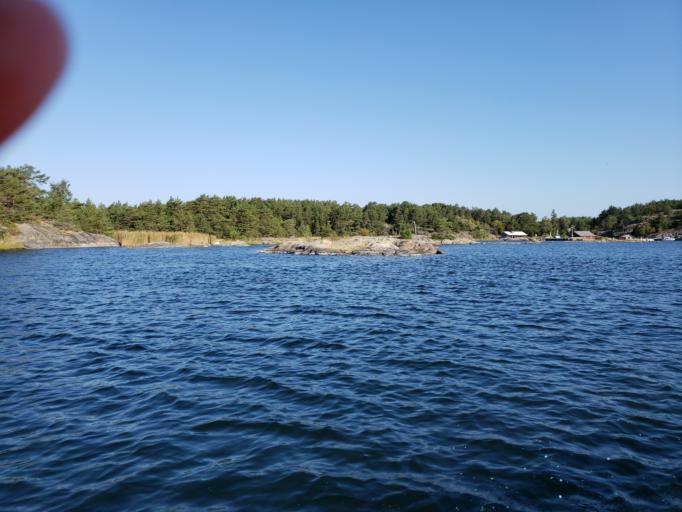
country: FI
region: Varsinais-Suomi
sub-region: Aboland-Turunmaa
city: Dragsfjaerd
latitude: 59.9051
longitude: 22.3667
